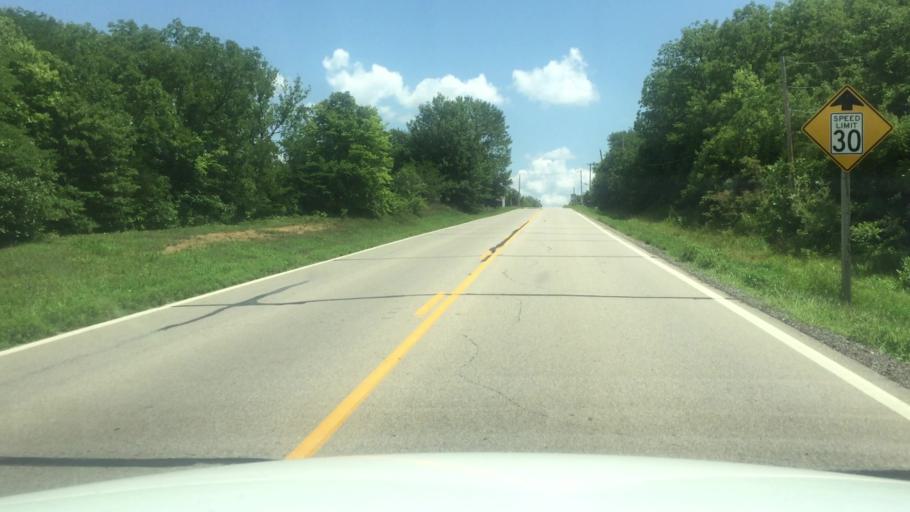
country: US
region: Kansas
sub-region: Brown County
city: Horton
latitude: 39.6673
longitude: -95.5374
